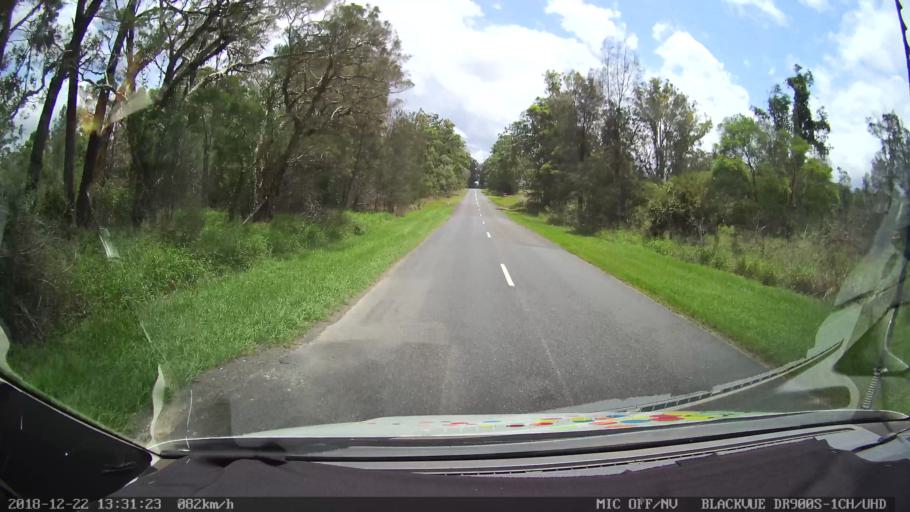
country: AU
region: New South Wales
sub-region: Clarence Valley
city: Coutts Crossing
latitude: -29.8553
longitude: 152.8535
